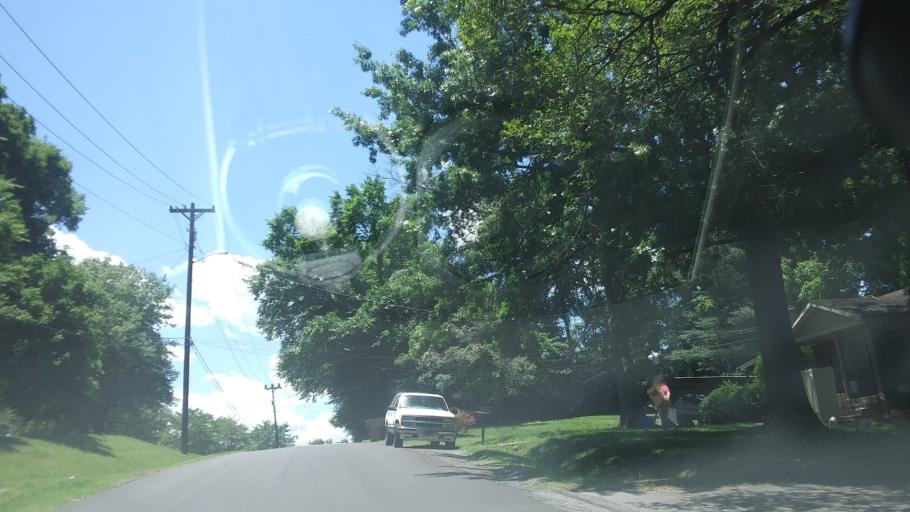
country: US
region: Tennessee
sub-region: Davidson County
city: Oak Hill
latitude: 36.0817
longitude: -86.6912
